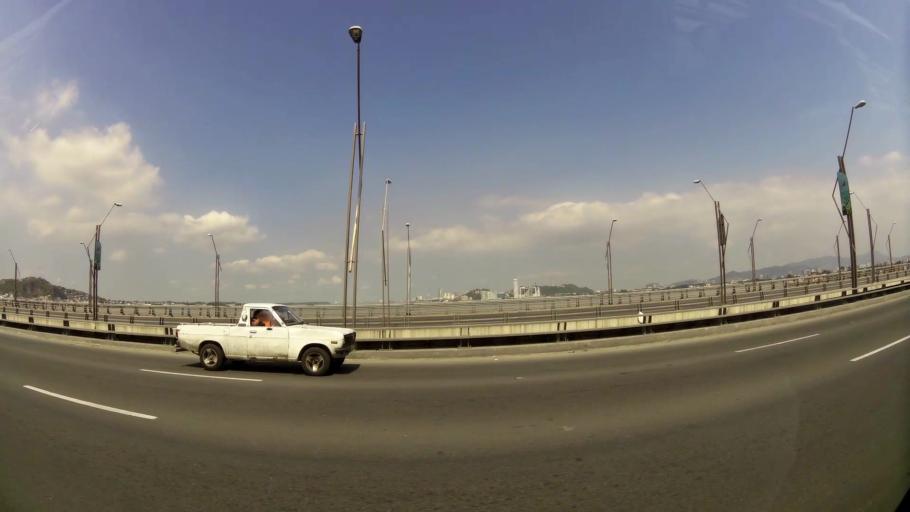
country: EC
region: Guayas
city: Eloy Alfaro
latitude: -2.1572
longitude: -79.8567
